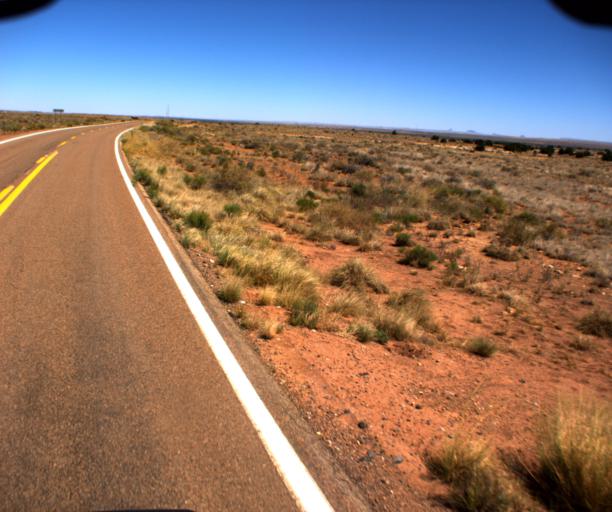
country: US
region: Arizona
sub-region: Navajo County
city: Winslow
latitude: 34.9419
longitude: -110.6441
